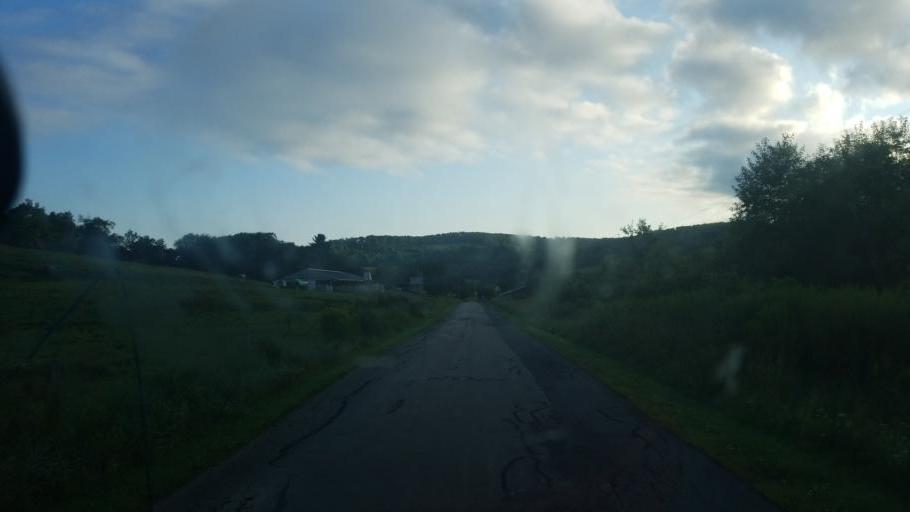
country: US
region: Pennsylvania
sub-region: Potter County
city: Galeton
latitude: 41.8928
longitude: -77.8048
